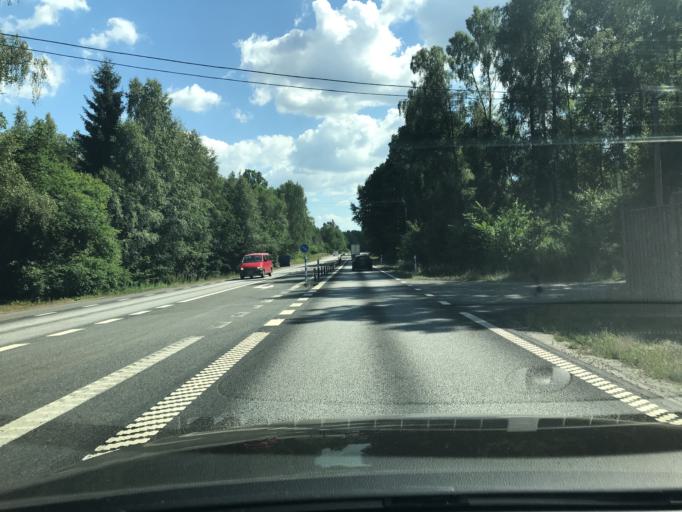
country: SE
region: Skane
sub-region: Osby Kommun
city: Osby
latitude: 56.3463
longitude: 14.0107
